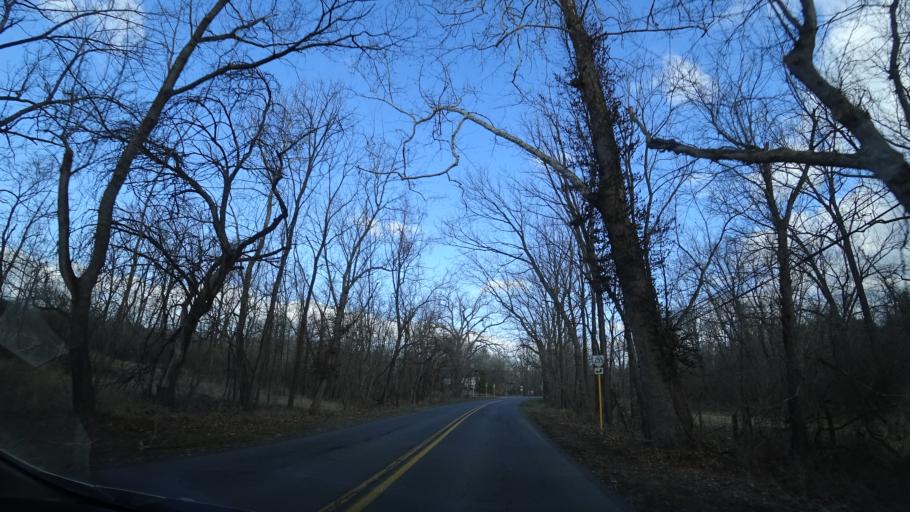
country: US
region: Virginia
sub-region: Warren County
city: Shenandoah Farms
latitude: 39.0663
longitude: -78.0368
